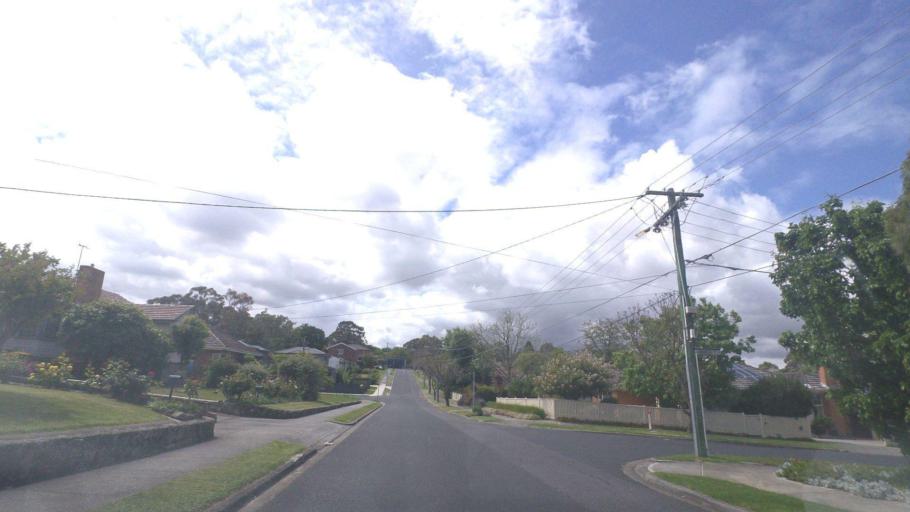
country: AU
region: Victoria
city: Rosanna
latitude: -37.7430
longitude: 145.0702
